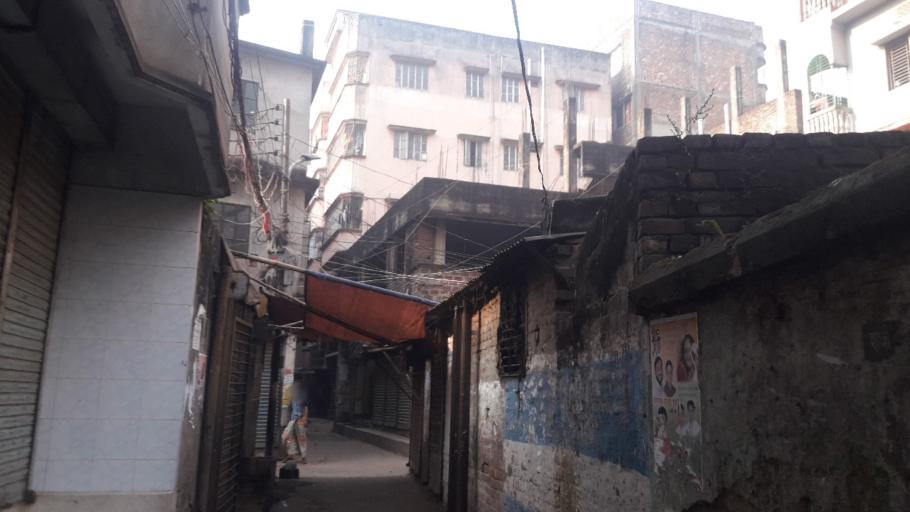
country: BD
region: Dhaka
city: Azimpur
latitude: 23.7231
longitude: 90.3763
